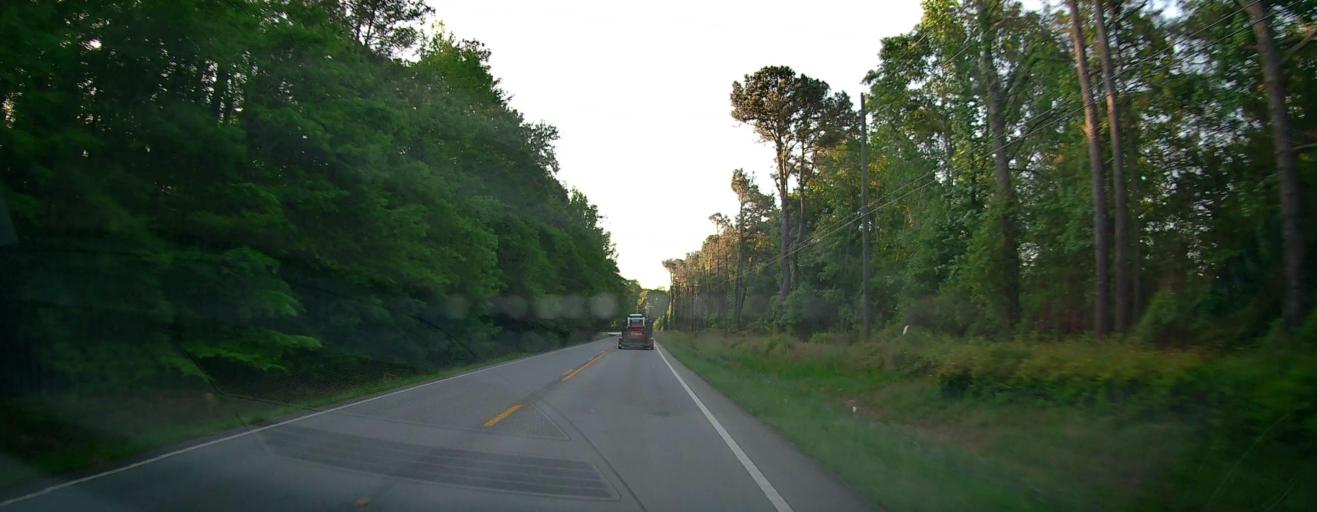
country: US
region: Georgia
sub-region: Walton County
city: Social Circle
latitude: 33.5418
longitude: -83.7269
